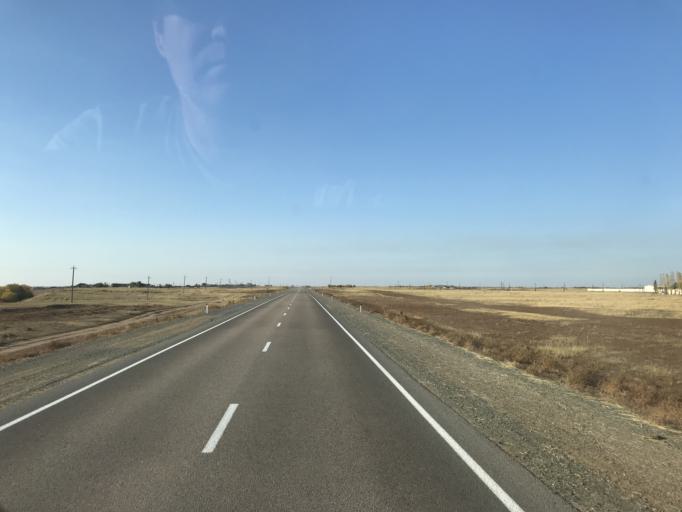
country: KZ
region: Pavlodar
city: Koktobe
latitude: 51.6385
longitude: 77.5934
